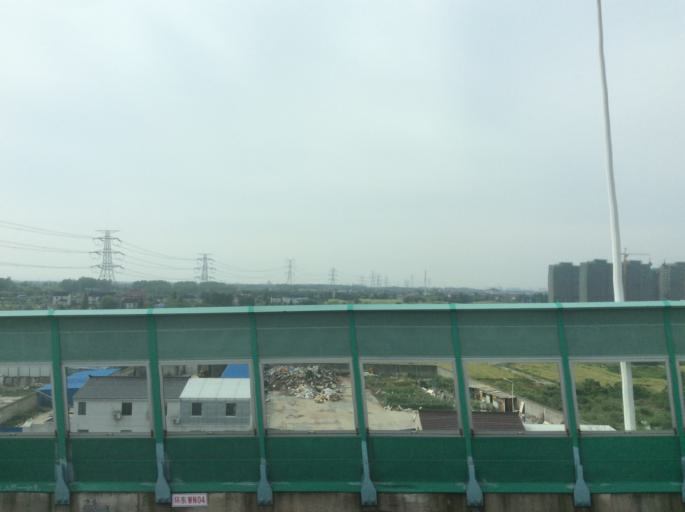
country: CN
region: Shanghai Shi
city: Kangqiao
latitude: 31.1906
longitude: 121.6382
